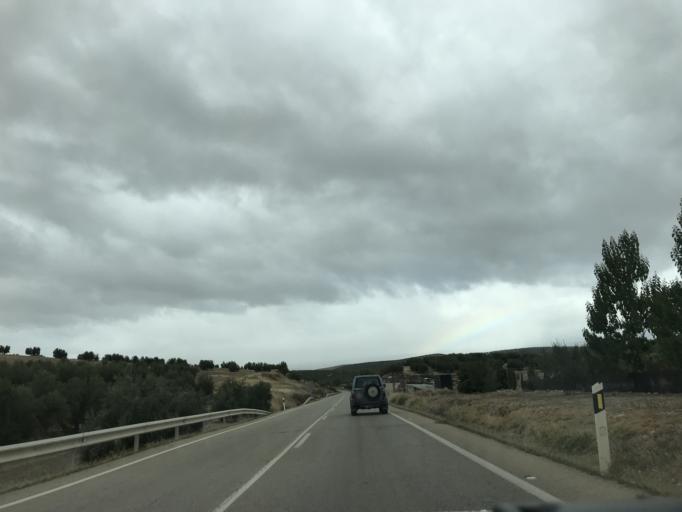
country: ES
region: Andalusia
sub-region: Provincia de Jaen
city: Peal de Becerro
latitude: 37.9219
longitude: -3.1330
